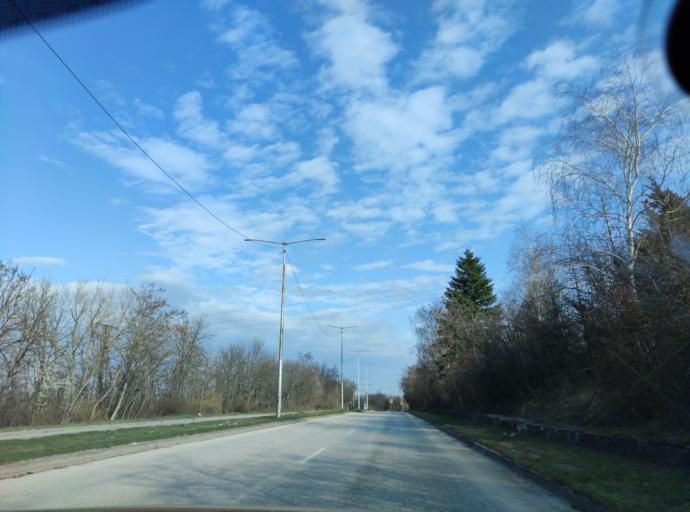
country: BG
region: Pleven
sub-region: Obshtina Dolna Mitropoliya
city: Dolna Mitropoliya
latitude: 43.4346
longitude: 24.5697
